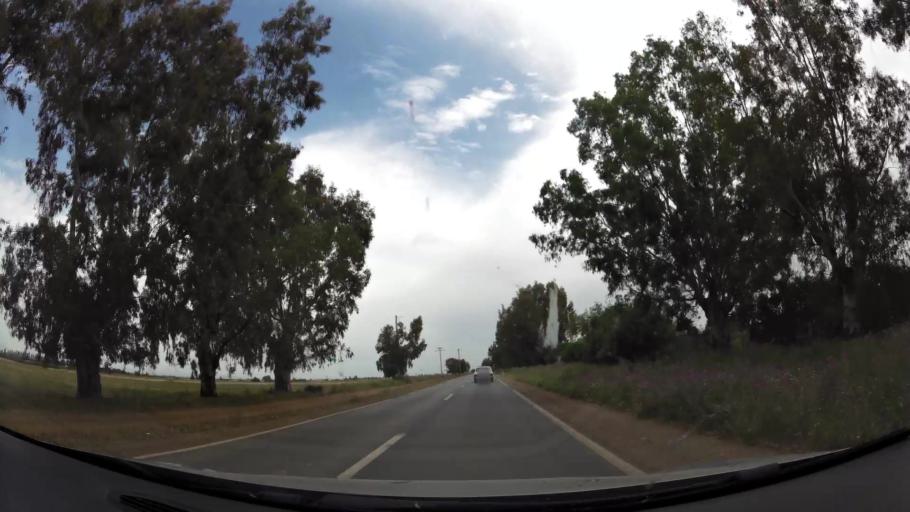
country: MA
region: Rabat-Sale-Zemmour-Zaer
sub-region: Khemisset
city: Tiflet
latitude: 33.8197
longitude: -6.2724
